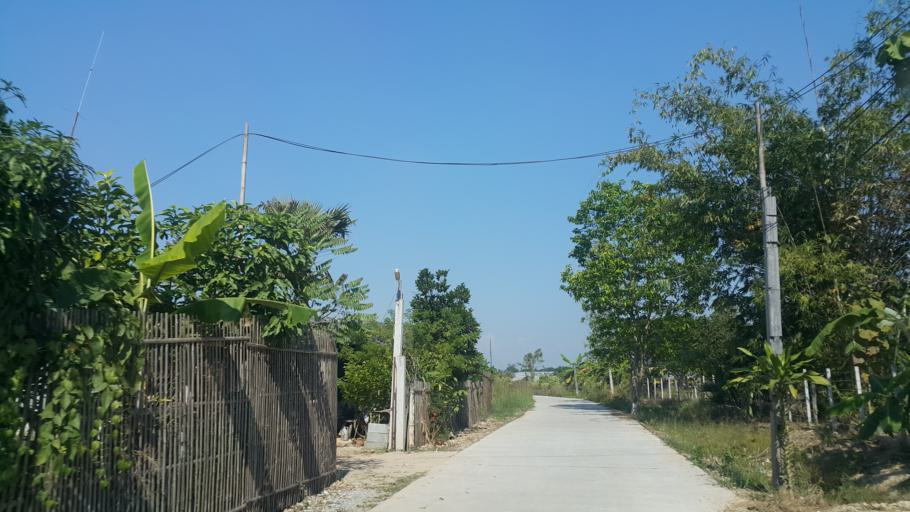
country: TH
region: Chiang Mai
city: San Kamphaeng
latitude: 18.6894
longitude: 99.1667
